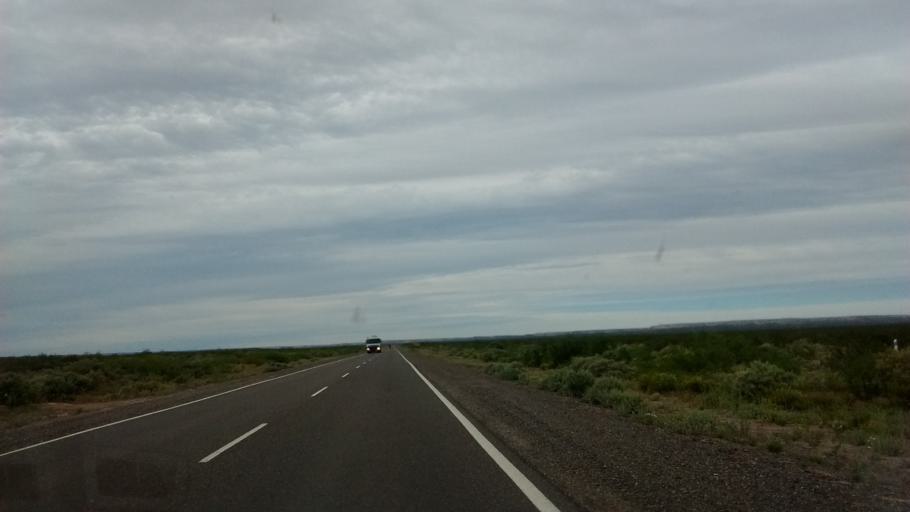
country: AR
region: Rio Negro
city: Catriel
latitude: -38.0761
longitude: -67.9240
